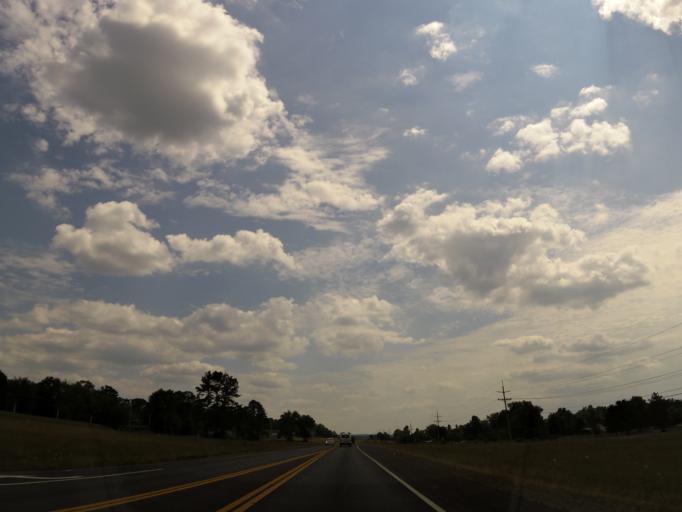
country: US
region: Tennessee
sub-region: Marion County
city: Whitwell
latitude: 35.1680
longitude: -85.5348
